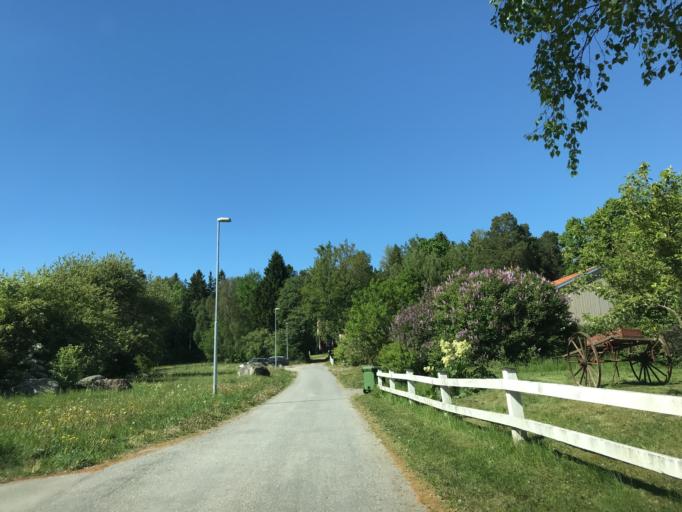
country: SE
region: Stockholm
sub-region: Upplands Vasby Kommun
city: Upplands Vaesby
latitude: 59.4644
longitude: 17.8926
